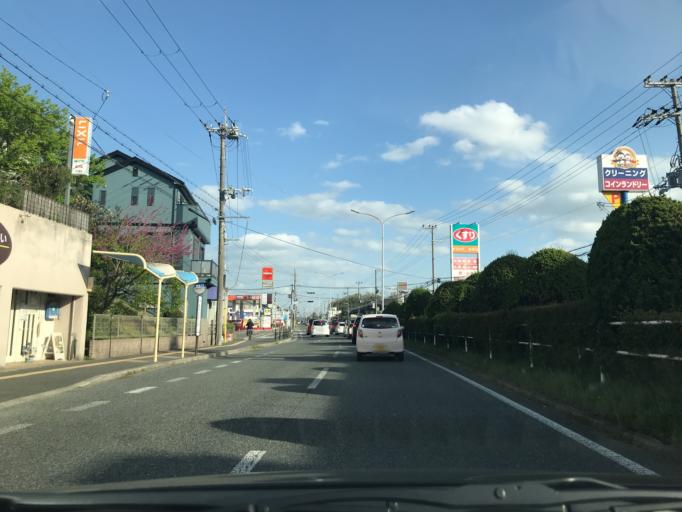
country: JP
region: Hyogo
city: Kawanishi
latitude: 34.8721
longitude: 135.3879
